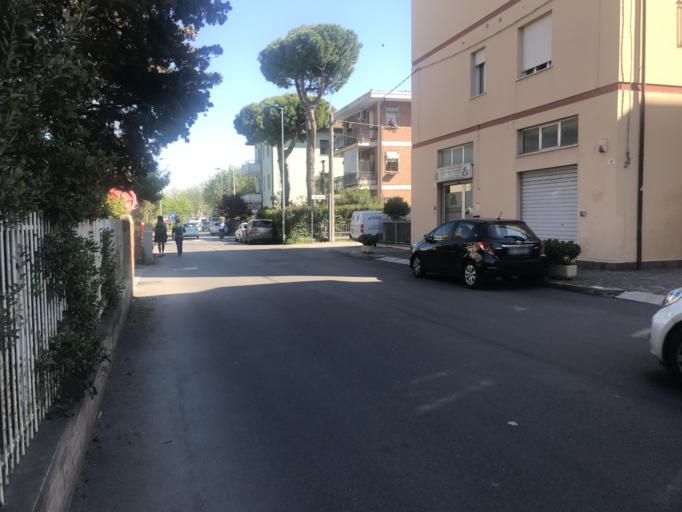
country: IT
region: Emilia-Romagna
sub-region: Provincia di Rimini
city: Rimini
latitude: 44.0518
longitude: 12.5828
